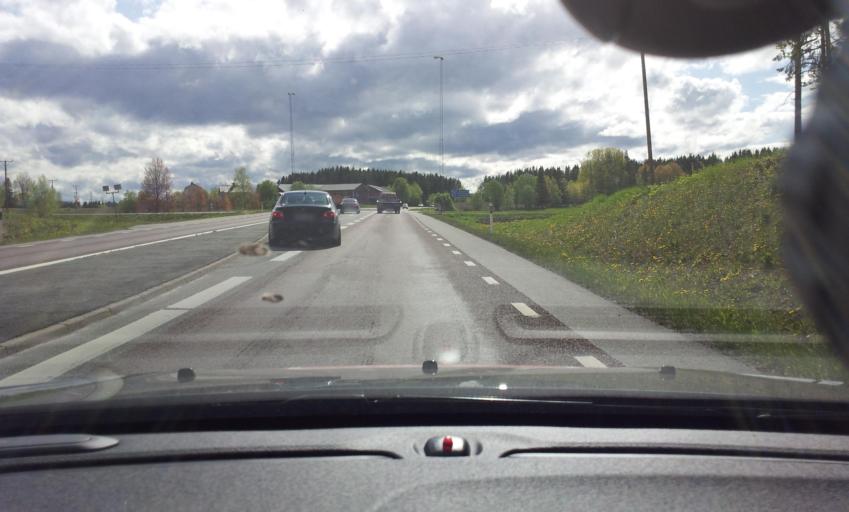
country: SE
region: Jaemtland
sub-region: OEstersunds Kommun
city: Brunflo
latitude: 63.0182
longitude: 14.7356
